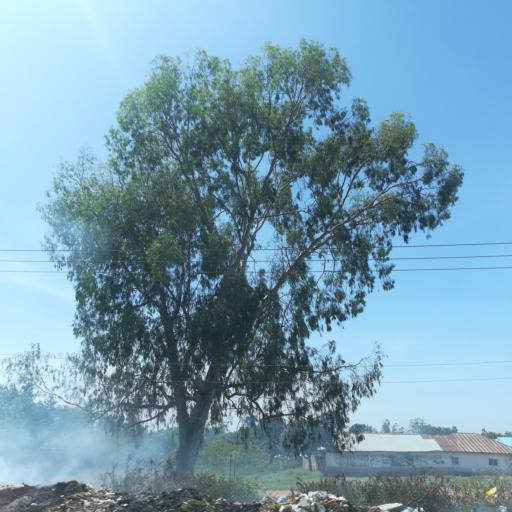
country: NG
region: Plateau
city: Bukuru
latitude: 9.7875
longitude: 8.8768
